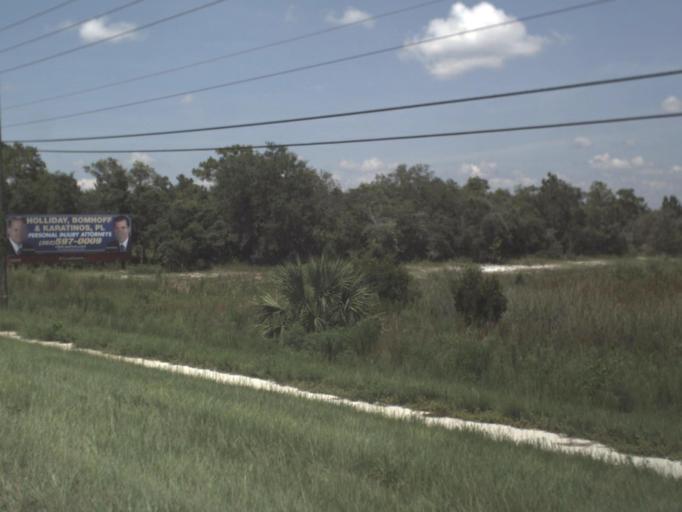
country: US
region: Florida
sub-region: Hernando County
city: North Weeki Wachee
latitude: 28.5537
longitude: -82.5622
